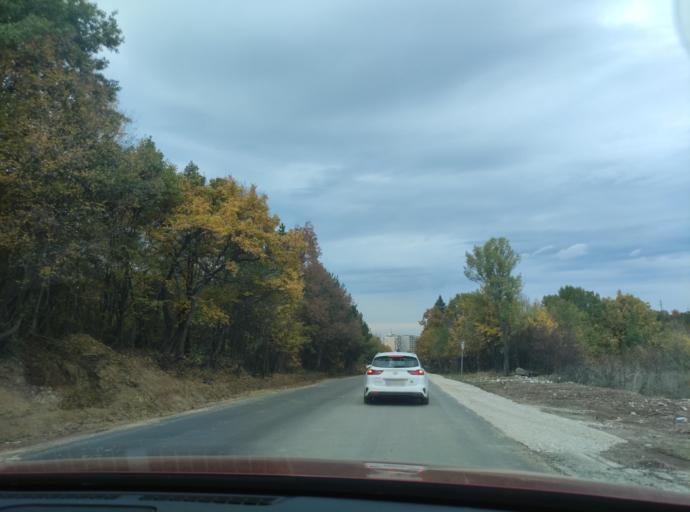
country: BG
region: Montana
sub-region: Obshtina Montana
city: Montana
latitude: 43.3921
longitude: 23.2414
